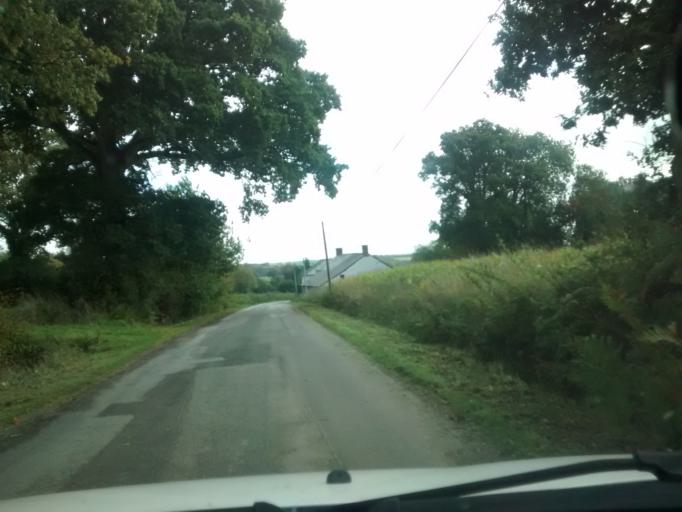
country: FR
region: Brittany
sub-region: Departement d'Ille-et-Vilaine
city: Chateaubourg
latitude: 48.1291
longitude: -1.4038
